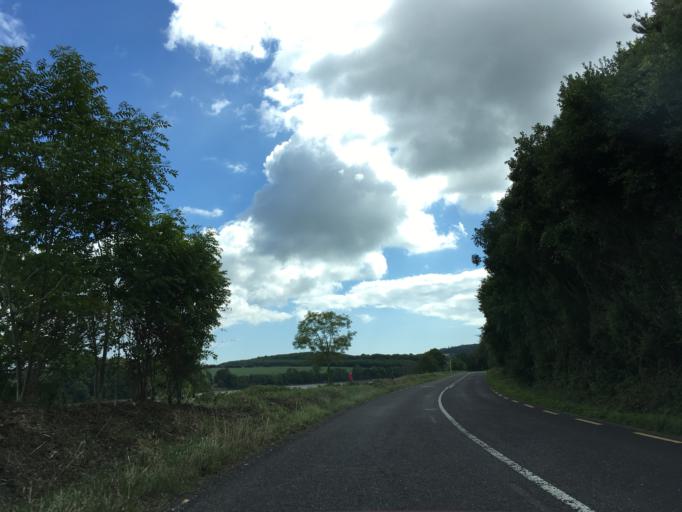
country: IE
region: Munster
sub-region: County Cork
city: Carrigaline
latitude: 51.8097
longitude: -8.3506
